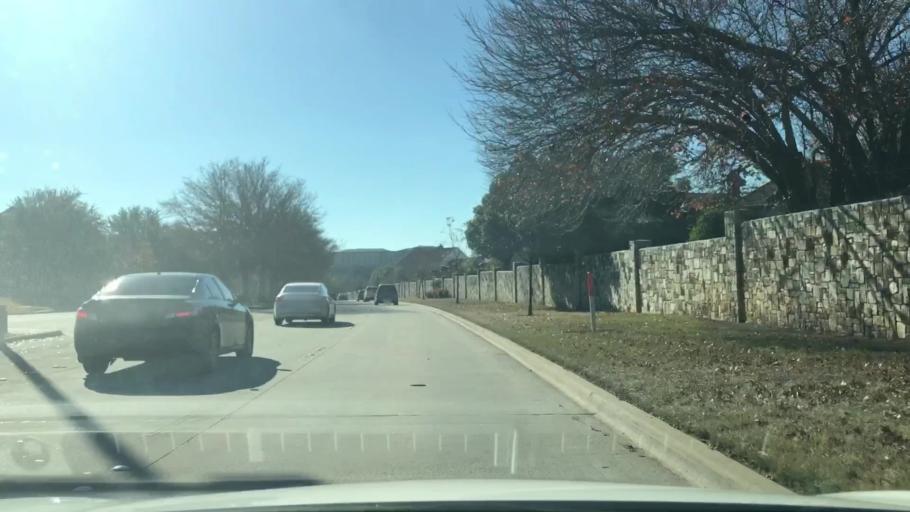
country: US
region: Texas
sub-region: Denton County
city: The Colony
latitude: 33.0983
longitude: -96.8421
